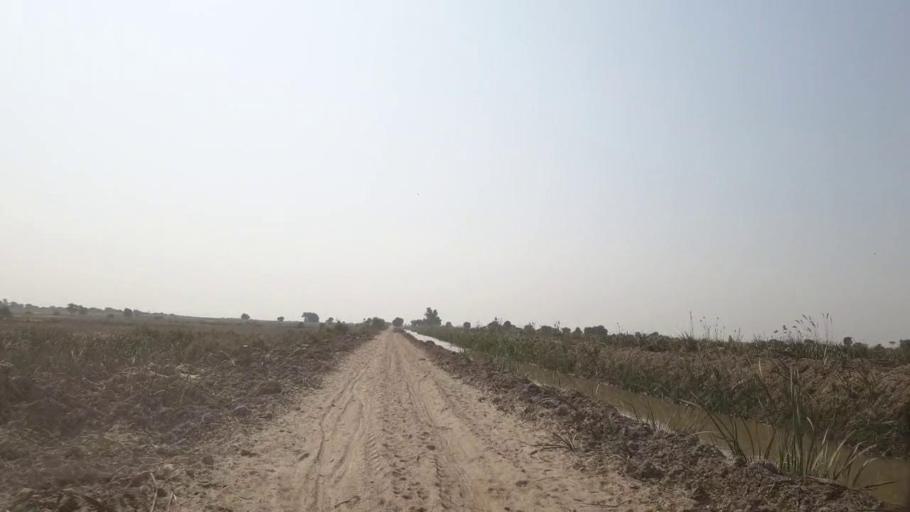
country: PK
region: Sindh
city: Bulri
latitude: 24.9793
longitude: 68.4038
